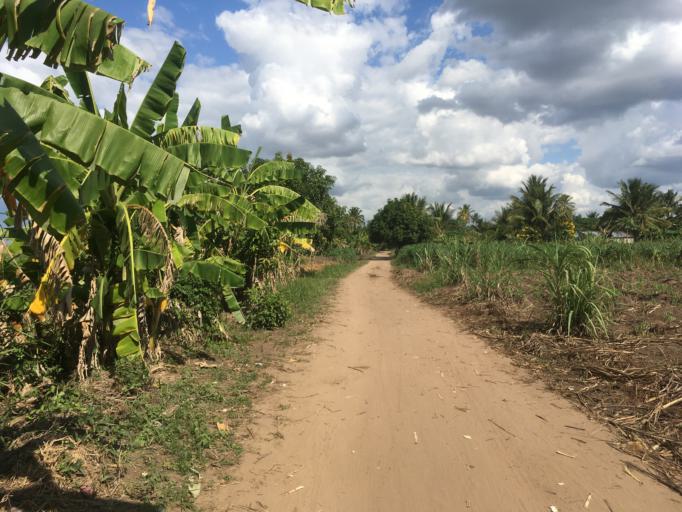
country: MZ
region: Zambezia
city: Quelimane
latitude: -17.6429
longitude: 36.6860
